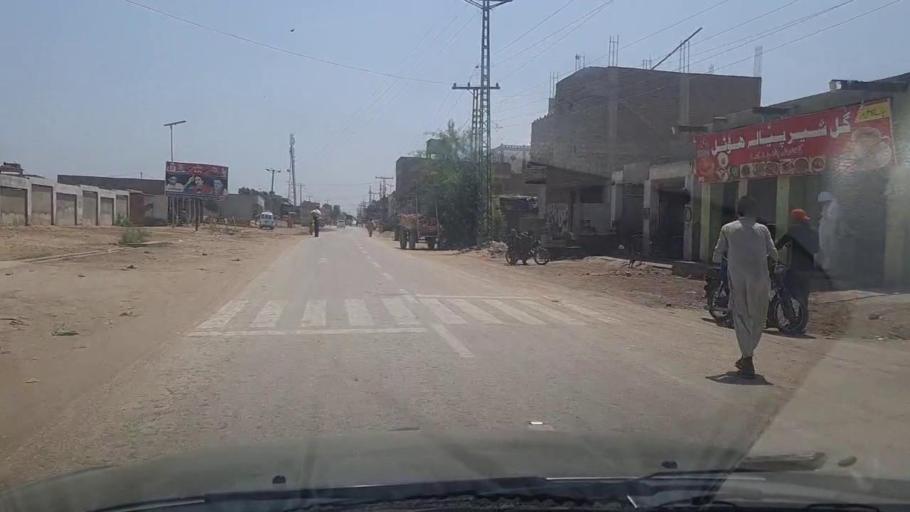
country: PK
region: Sindh
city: Hyderabad
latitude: 25.3878
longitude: 68.4251
